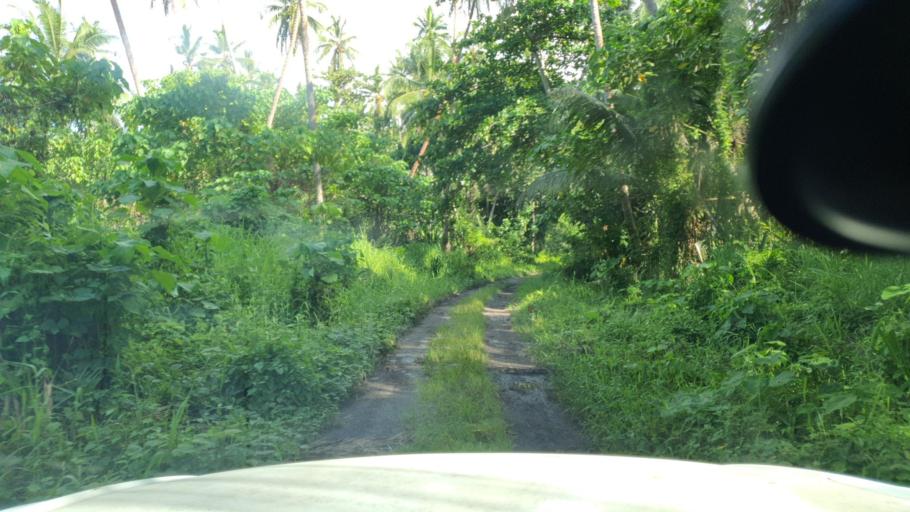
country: SB
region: Guadalcanal
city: Honiara
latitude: -9.2887
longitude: 159.7657
